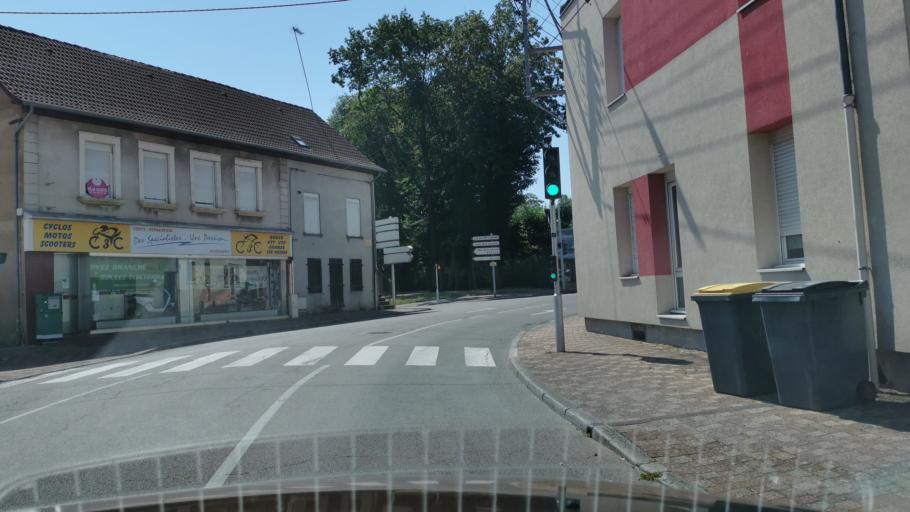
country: FR
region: Bourgogne
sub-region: Departement de Saone-et-Loire
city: Le Creusot
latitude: 46.8035
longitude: 4.4130
